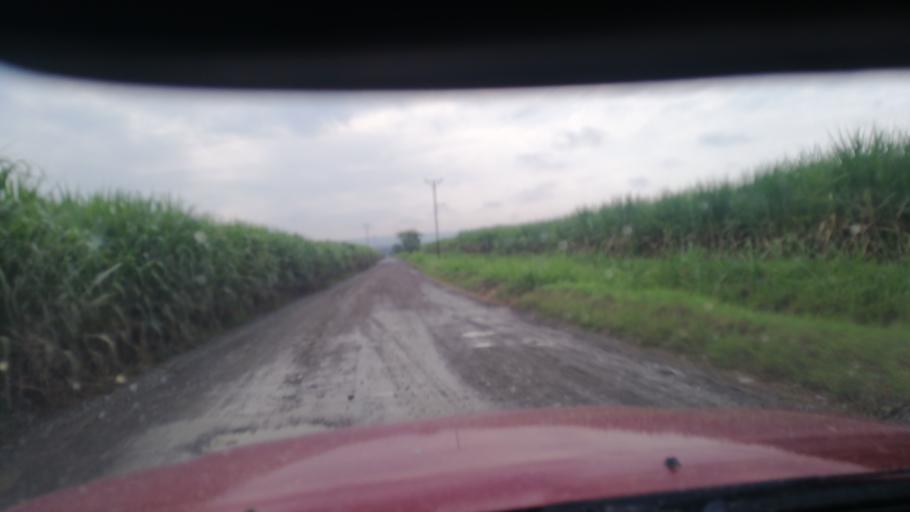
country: CO
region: Risaralda
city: La Virginia
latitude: 4.8773
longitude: -75.9278
